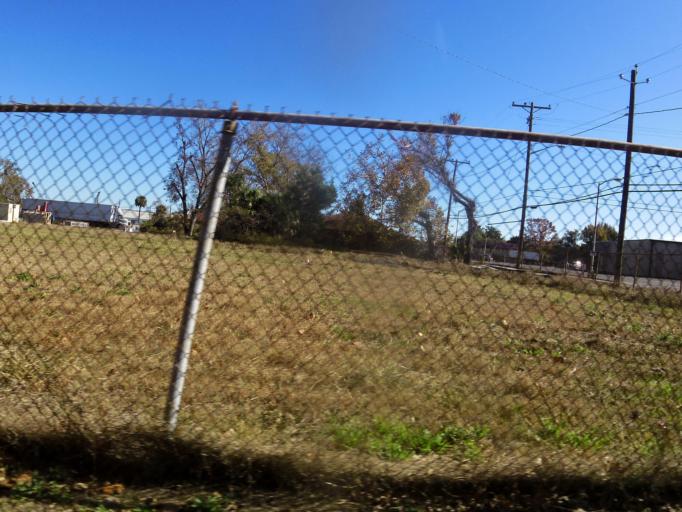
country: US
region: Georgia
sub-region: Chatham County
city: Savannah
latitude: 32.0723
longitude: -81.1159
